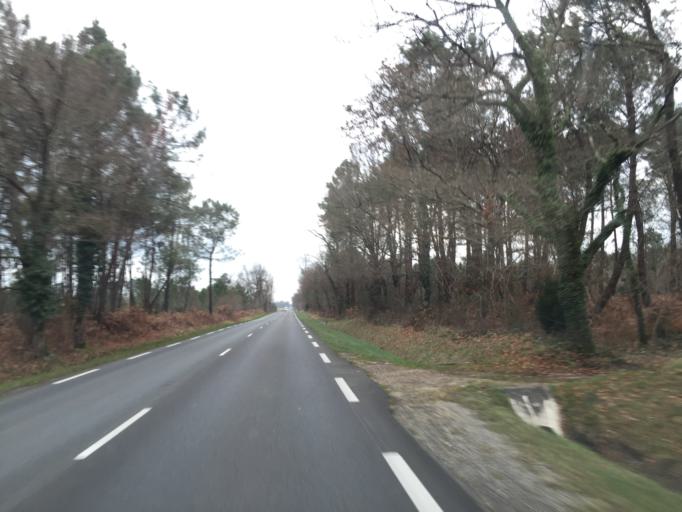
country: FR
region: Aquitaine
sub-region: Departement de la Gironde
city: Saint-Sauveur
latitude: 45.1922
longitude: -0.8526
